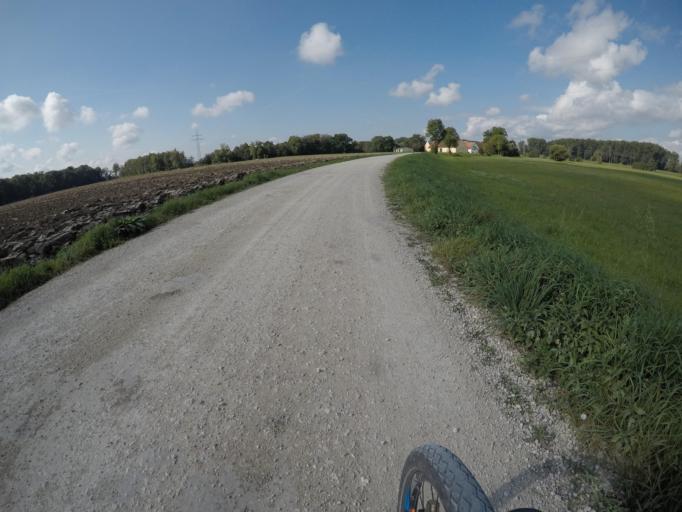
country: DE
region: Bavaria
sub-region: Swabia
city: Tapfheim
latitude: 48.6502
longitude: 10.7080
